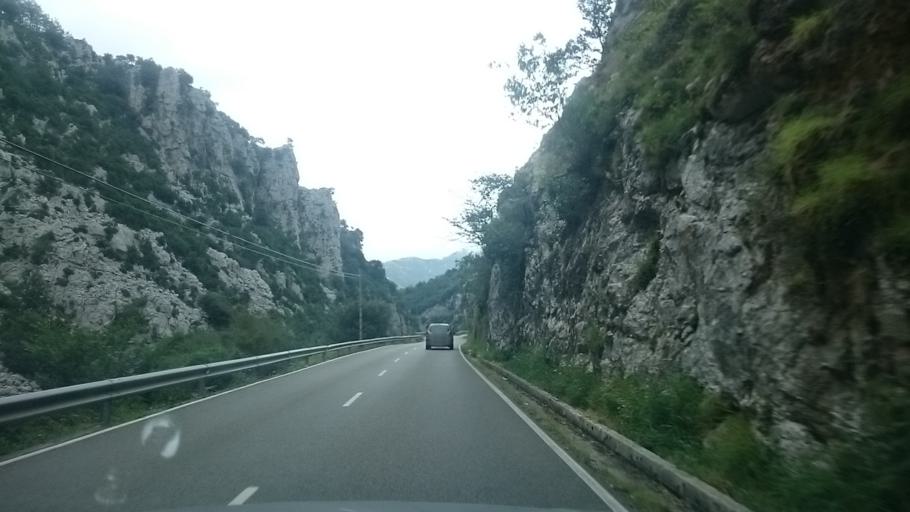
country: ES
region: Asturias
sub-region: Province of Asturias
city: Carrena
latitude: 43.2868
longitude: -4.8319
